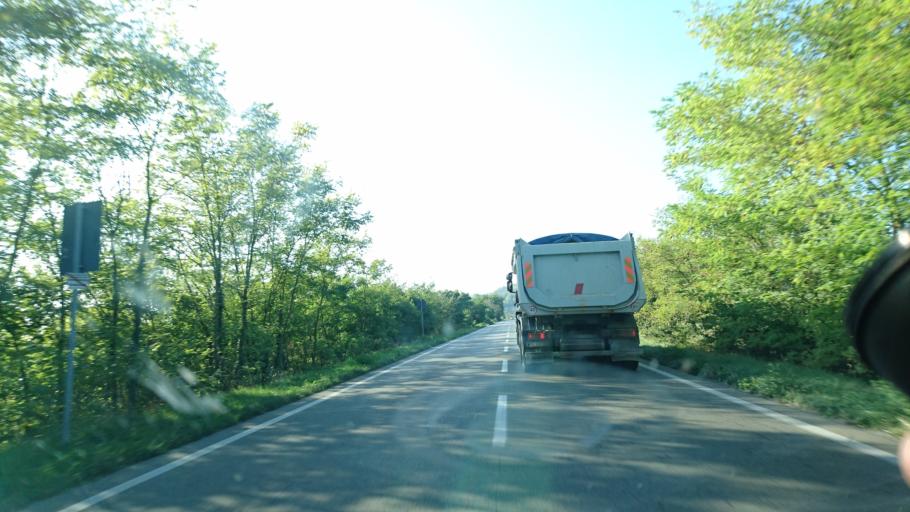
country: IT
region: Piedmont
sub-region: Provincia di Alessandria
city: Acqui Terme
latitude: 44.6713
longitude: 8.4483
